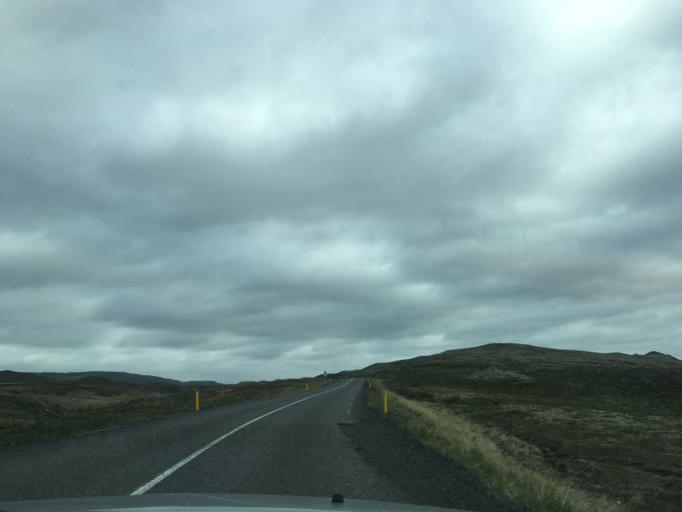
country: IS
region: South
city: Vestmannaeyjar
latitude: 64.2674
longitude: -20.1925
